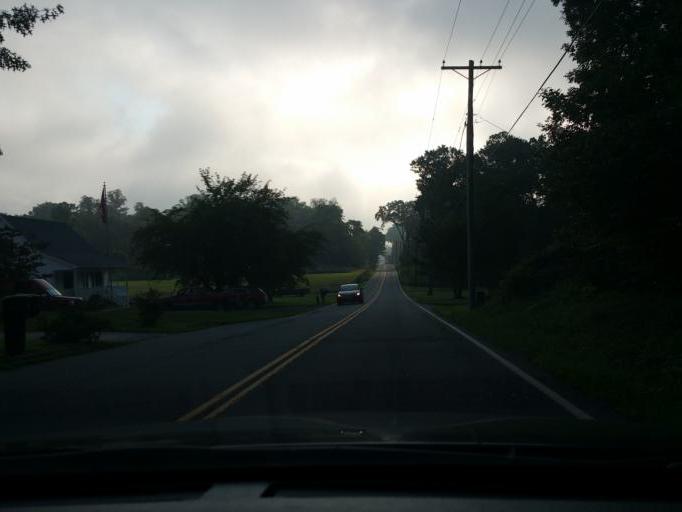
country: US
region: Maryland
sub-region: Cecil County
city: Rising Sun
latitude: 39.6738
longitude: -76.0818
